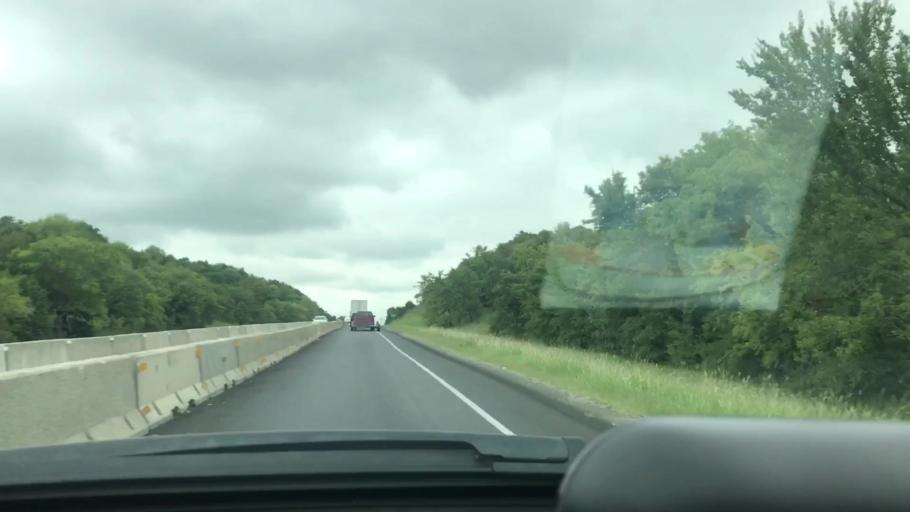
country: US
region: Oklahoma
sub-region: McIntosh County
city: Eufaula
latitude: 35.2692
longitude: -95.5915
